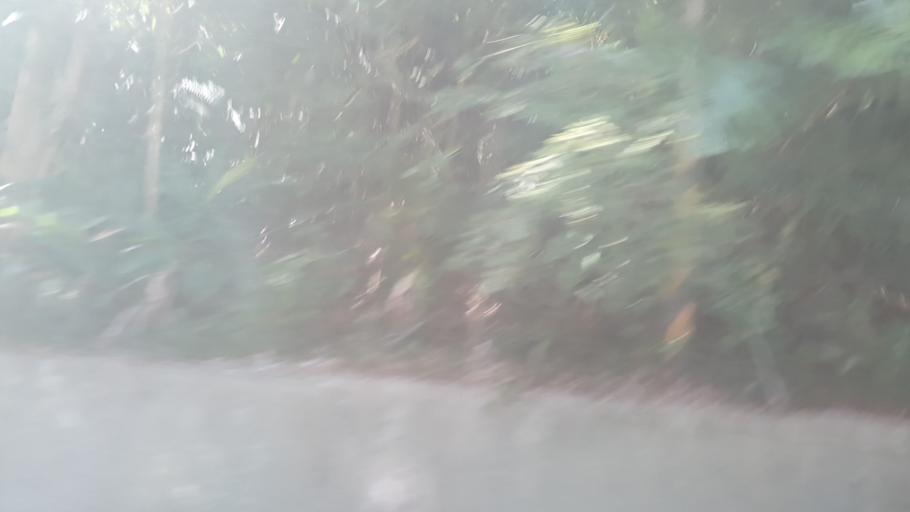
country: TW
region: Taiwan
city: Yujing
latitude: 23.0563
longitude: 120.3790
